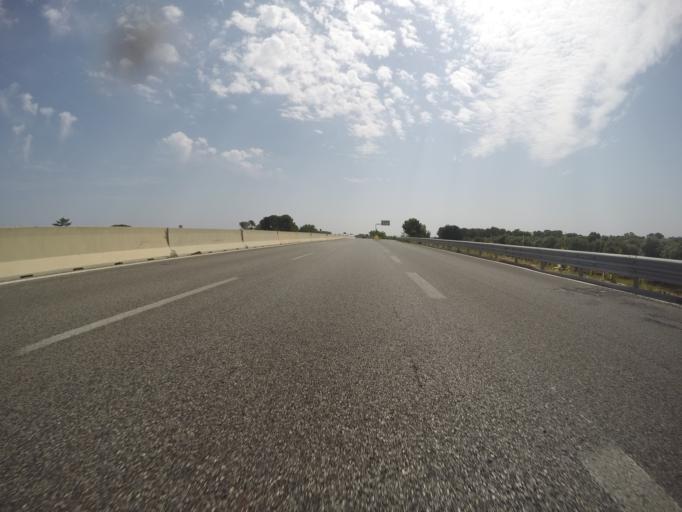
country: IT
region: Apulia
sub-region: Provincia di Brindisi
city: Mesagne
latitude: 40.5689
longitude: 17.7958
